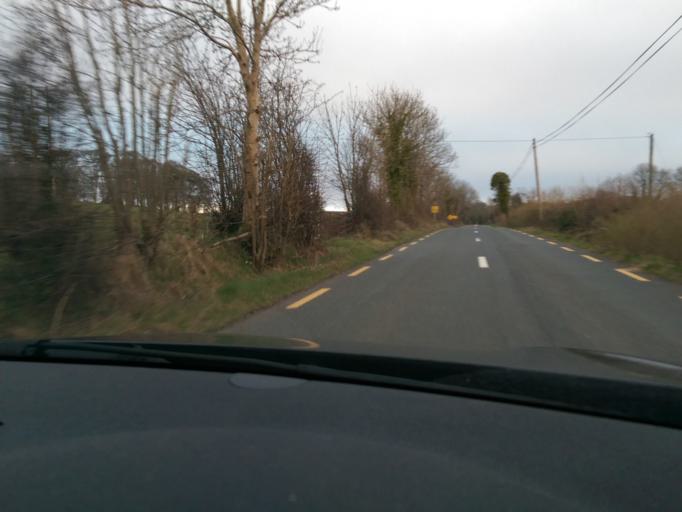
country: IE
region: Connaught
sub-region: Sligo
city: Ballymote
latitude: 54.0109
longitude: -8.5494
